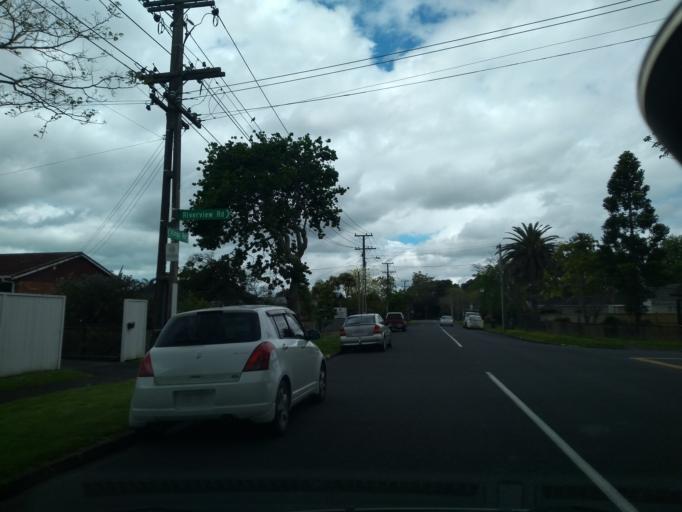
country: NZ
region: Auckland
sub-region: Auckland
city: Tamaki
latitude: -36.9022
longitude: 174.8630
